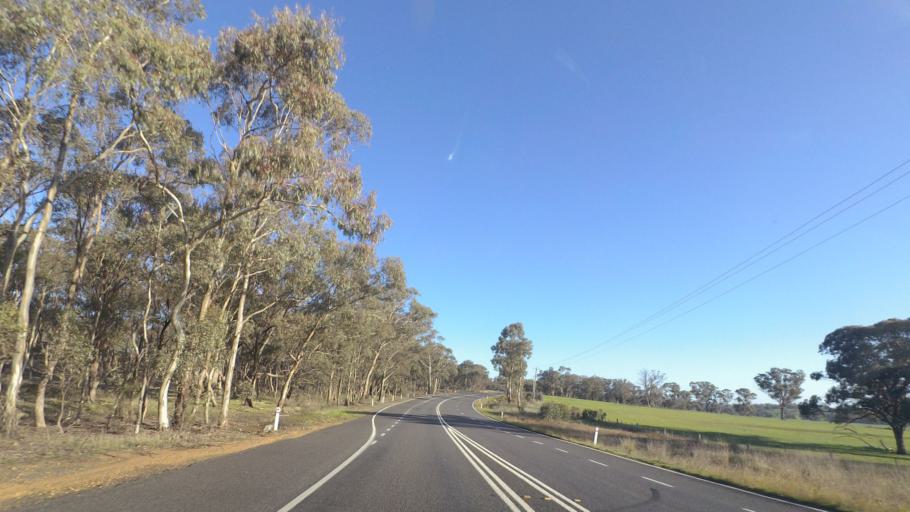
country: AU
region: Victoria
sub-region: Greater Bendigo
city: Kennington
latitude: -36.8579
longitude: 144.5054
